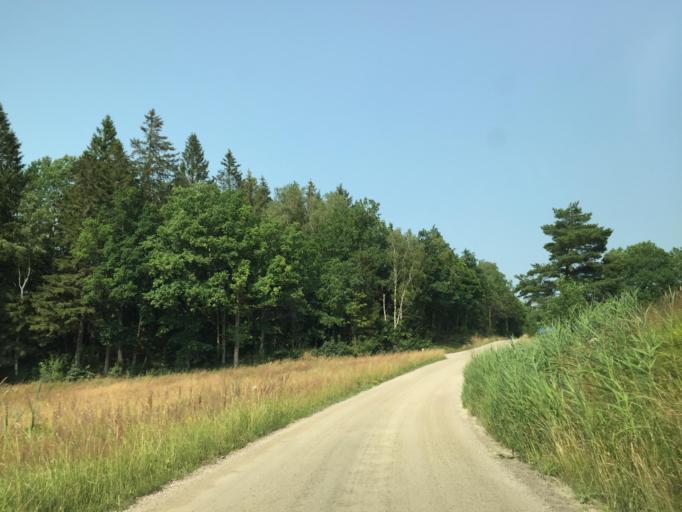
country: SE
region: Vaestra Goetaland
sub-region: Trollhattan
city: Sjuntorp
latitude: 58.2635
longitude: 12.0990
